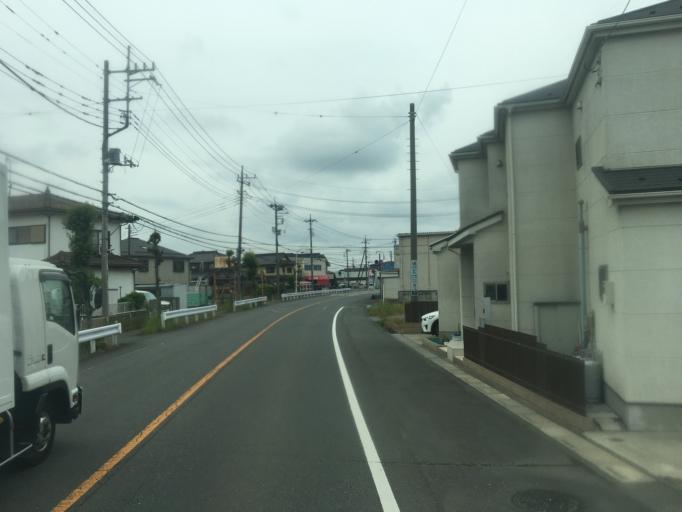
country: JP
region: Saitama
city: Kawagoe
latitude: 35.9759
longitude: 139.4610
